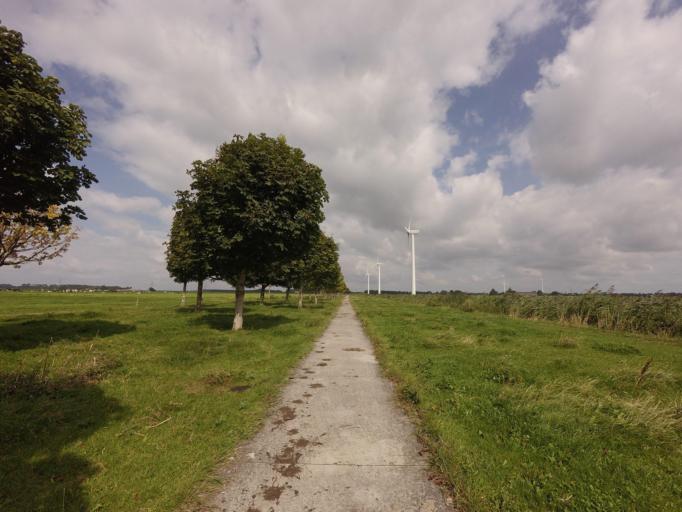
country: NL
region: Flevoland
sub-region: Gemeente Lelystad
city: Lelystad
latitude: 52.5647
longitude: 5.5554
